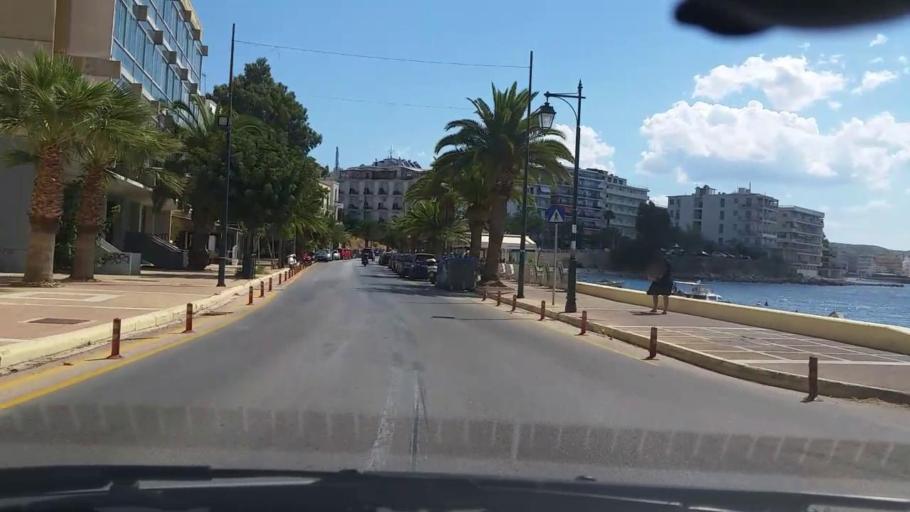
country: GR
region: Peloponnese
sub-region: Nomos Korinthias
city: Loutraki
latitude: 37.9825
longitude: 22.9707
